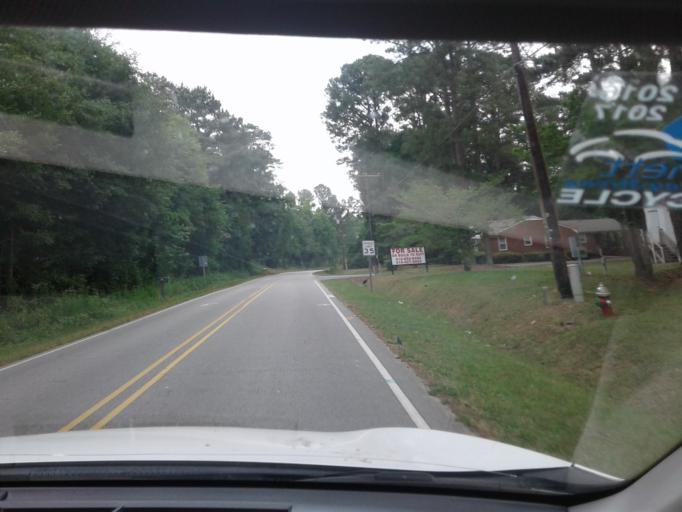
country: US
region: North Carolina
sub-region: Harnett County
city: Buies Creek
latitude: 35.4030
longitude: -78.7350
